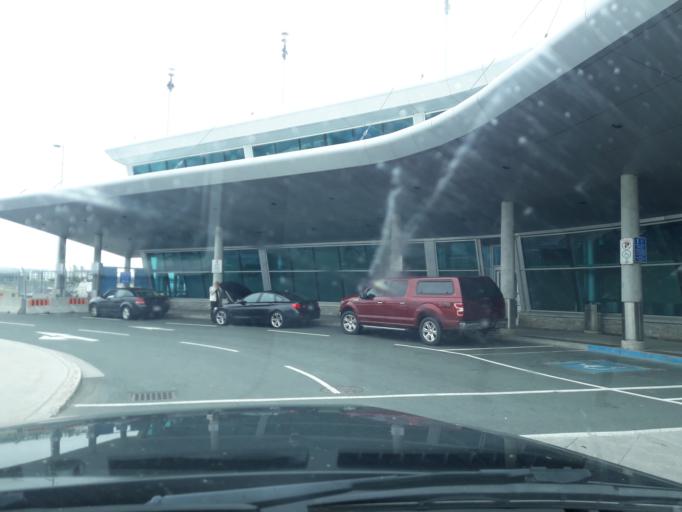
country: CA
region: Newfoundland and Labrador
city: Torbay
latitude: 47.6130
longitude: -52.7441
